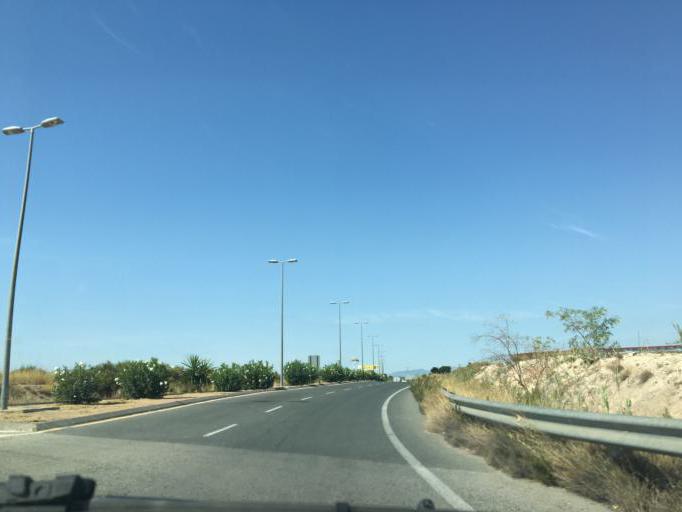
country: ES
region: Murcia
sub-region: Murcia
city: Murcia
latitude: 38.0436
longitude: -1.1368
